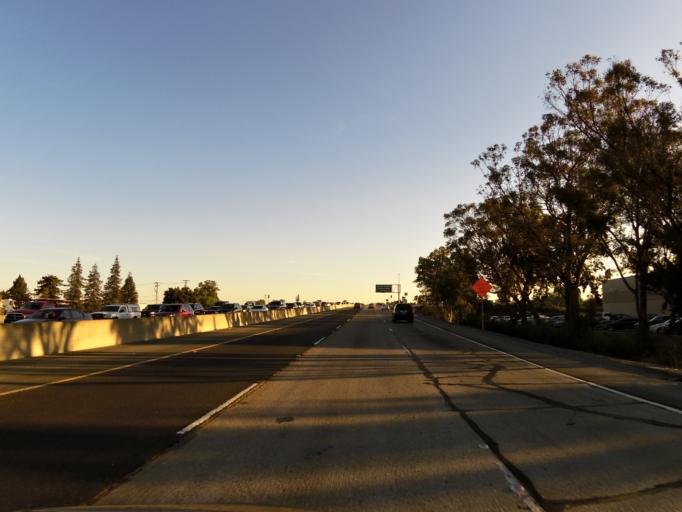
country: US
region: California
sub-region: Contra Costa County
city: Concord
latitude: 37.9770
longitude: -122.0443
